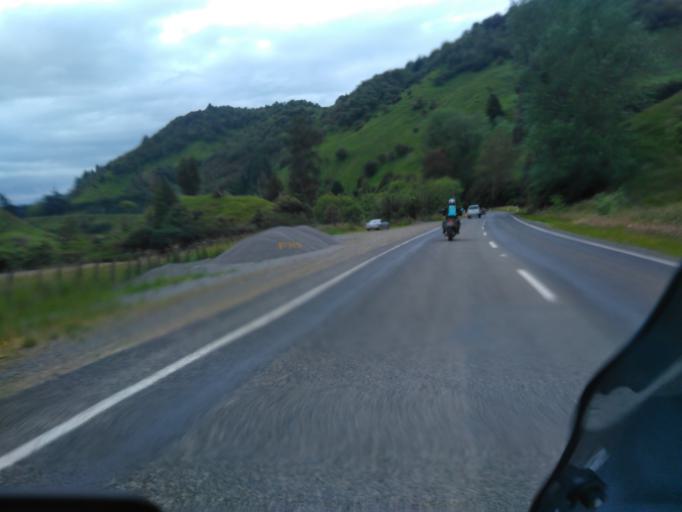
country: NZ
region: Bay of Plenty
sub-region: Opotiki District
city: Opotiki
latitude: -38.3754
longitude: 177.4846
